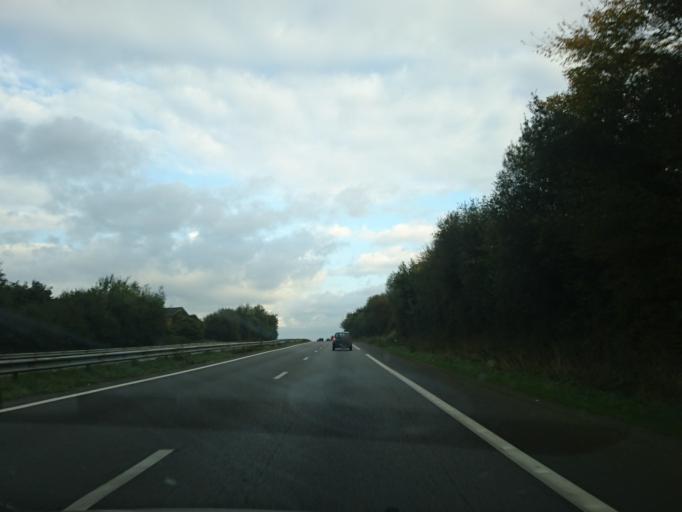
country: FR
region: Brittany
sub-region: Departement d'Ille-et-Vilaine
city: Montauban-de-Bretagne
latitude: 48.1858
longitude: -1.9976
